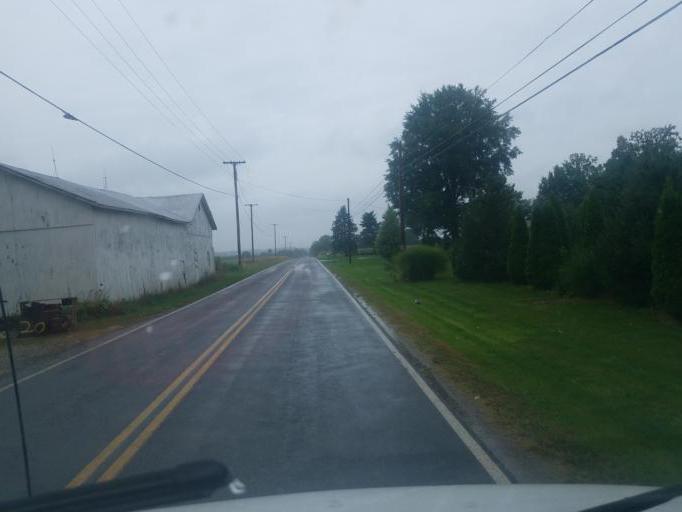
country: US
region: Ohio
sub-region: Medina County
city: Seville
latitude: 41.0100
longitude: -81.8333
